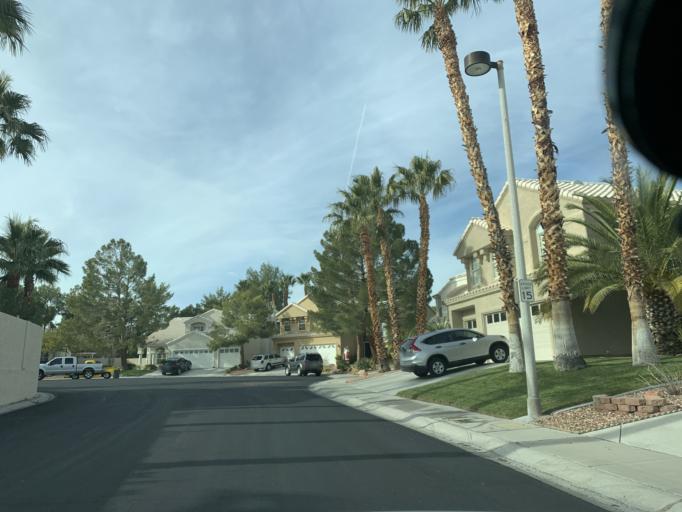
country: US
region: Nevada
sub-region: Clark County
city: Summerlin South
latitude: 36.1563
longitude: -115.2968
